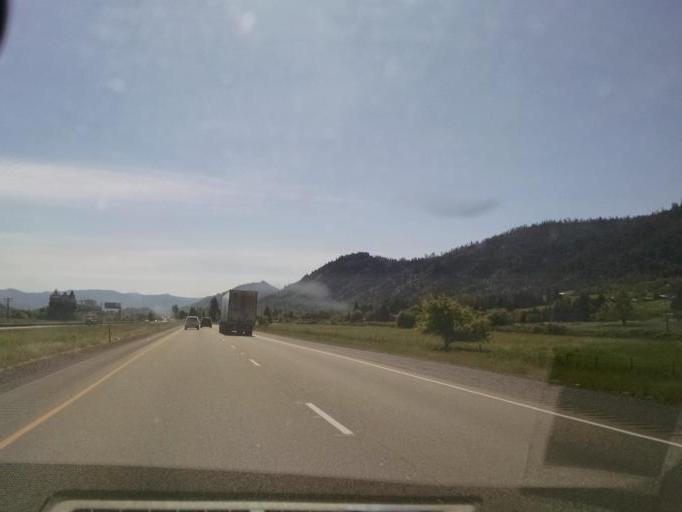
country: US
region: Oregon
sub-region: Douglas County
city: Tri-City
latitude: 43.0012
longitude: -123.3153
